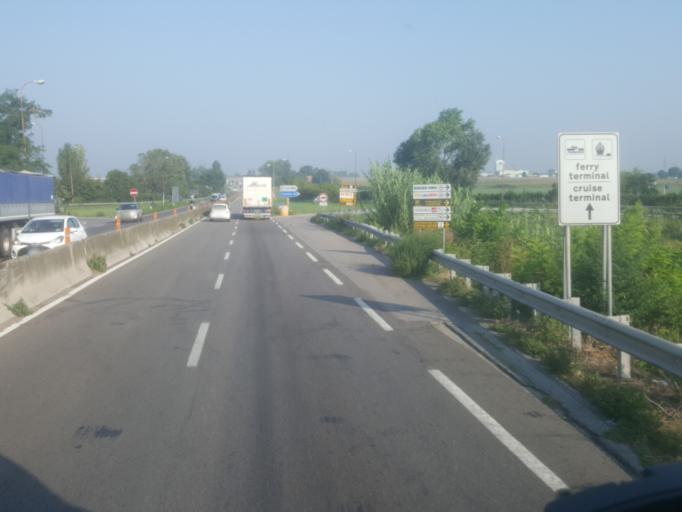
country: IT
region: Emilia-Romagna
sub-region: Provincia di Ravenna
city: Fornace Zarattini
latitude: 44.4229
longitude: 12.1617
